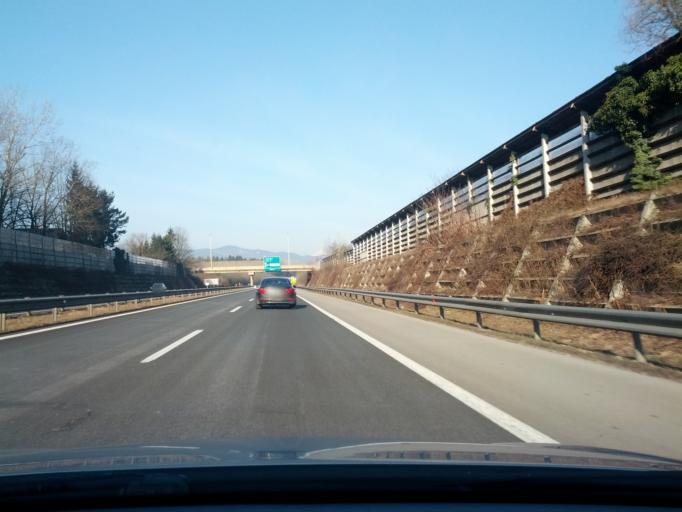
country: SI
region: Kranj
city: Kokrica
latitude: 46.2620
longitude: 14.3568
